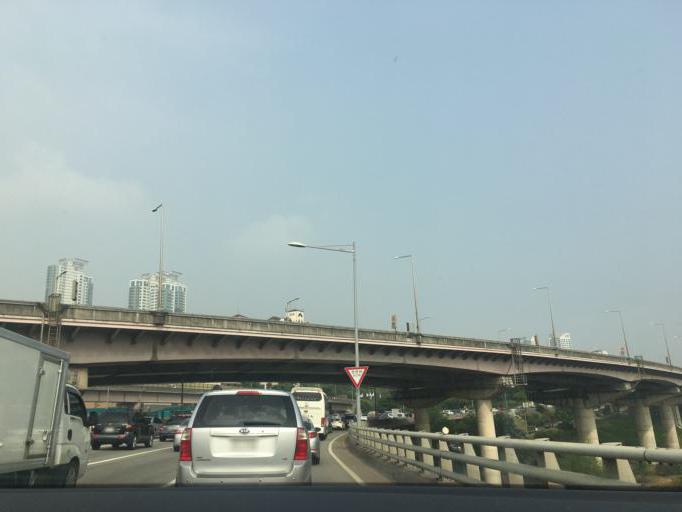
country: KR
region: Seoul
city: Seoul
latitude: 37.5186
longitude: 127.0669
